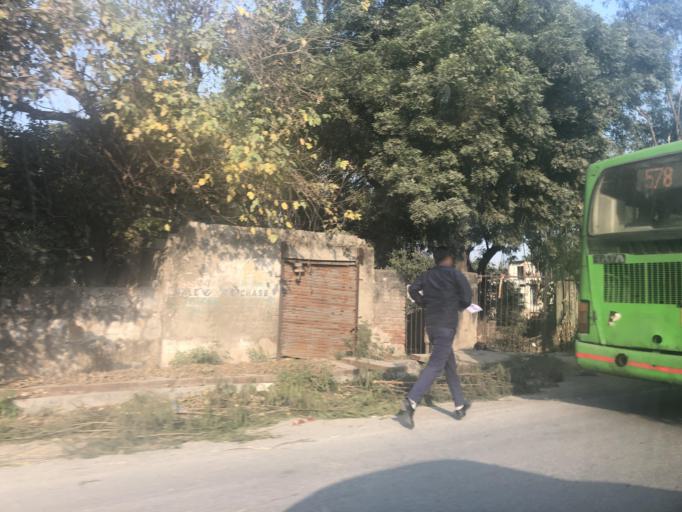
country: IN
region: Haryana
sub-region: Gurgaon
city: Gurgaon
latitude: 28.5404
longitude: 77.0253
